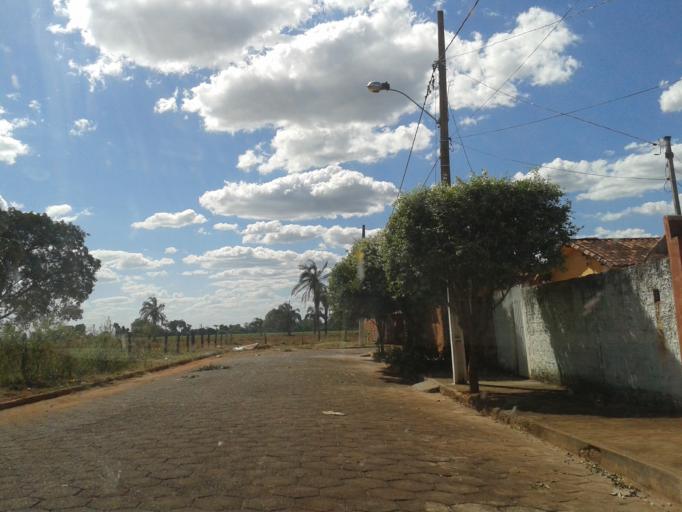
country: BR
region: Minas Gerais
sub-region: Santa Vitoria
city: Santa Vitoria
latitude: -18.6914
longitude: -49.9492
